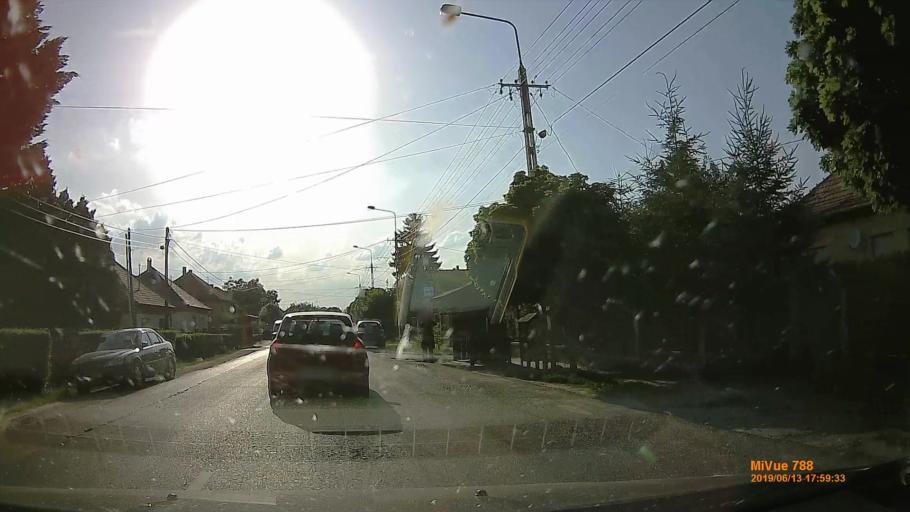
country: HU
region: Pest
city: Ecser
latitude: 47.4445
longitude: 19.3136
